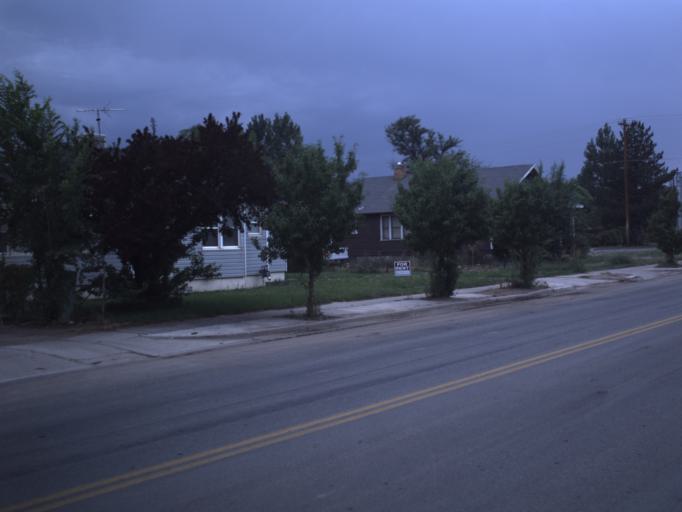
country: US
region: Utah
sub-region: Duchesne County
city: Roosevelt
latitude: 40.3022
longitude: -109.9910
